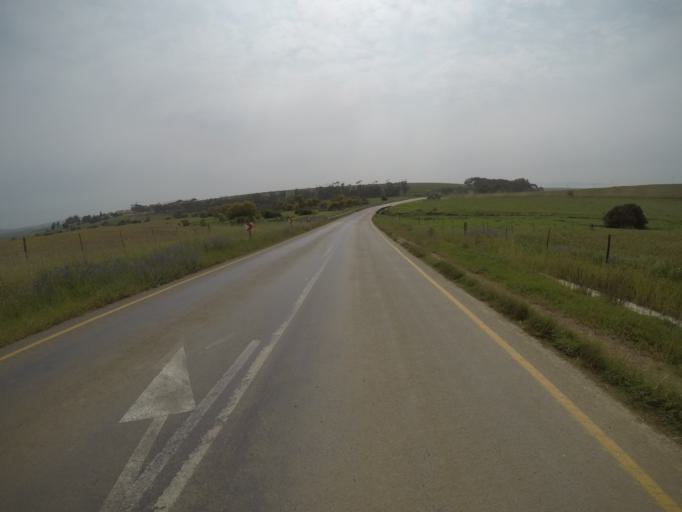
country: ZA
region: Western Cape
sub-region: City of Cape Town
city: Kraaifontein
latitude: -33.7311
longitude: 18.6342
